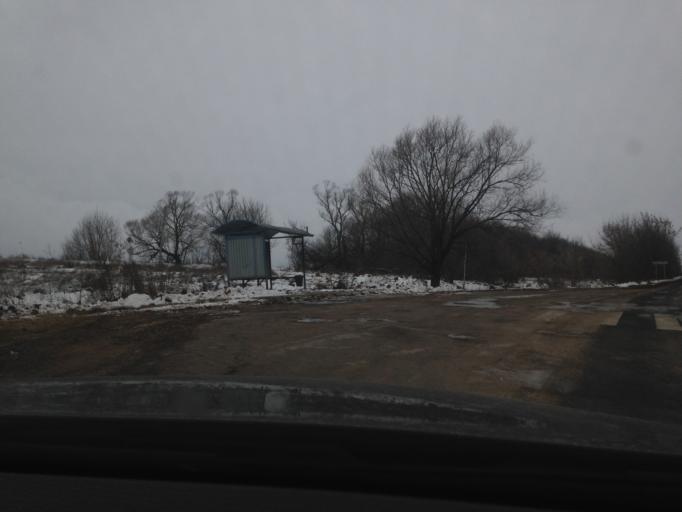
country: RU
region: Tula
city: Teploye
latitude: 53.7766
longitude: 37.6373
